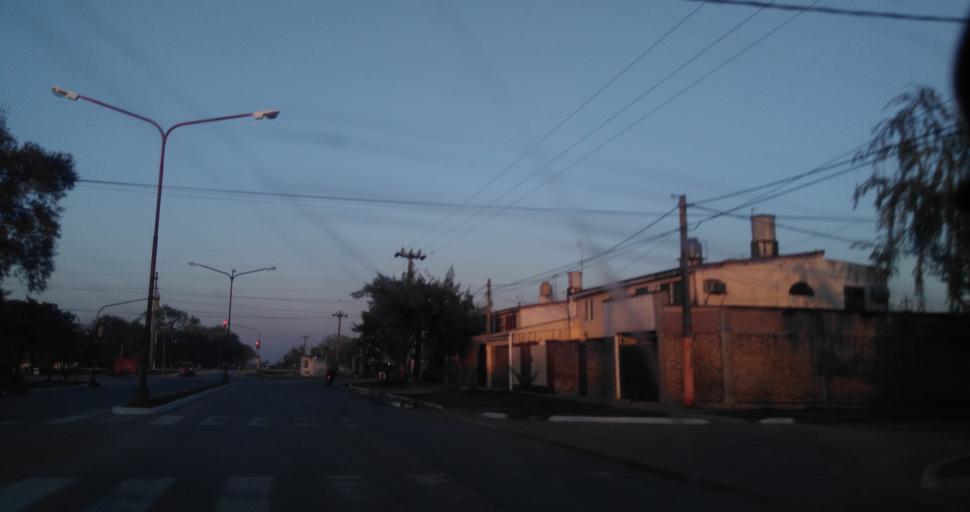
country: AR
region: Chaco
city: Resistencia
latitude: -27.4889
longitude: -58.9858
